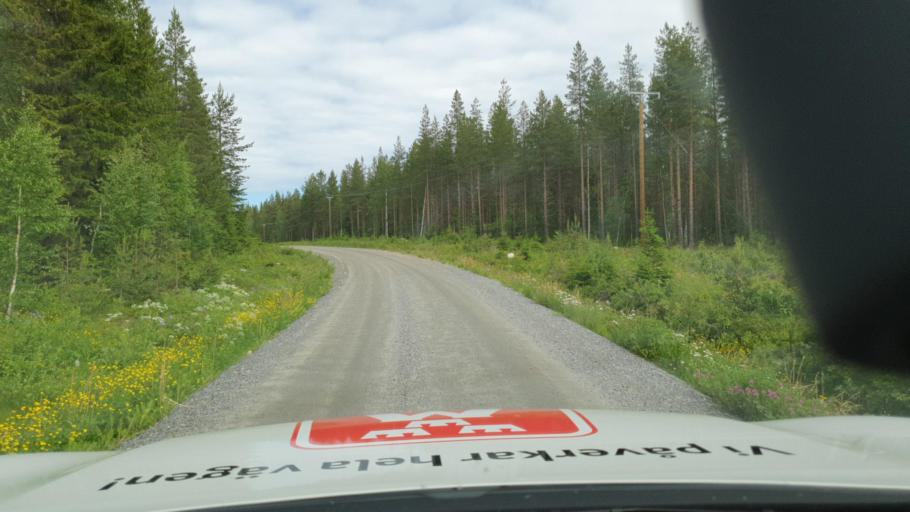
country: SE
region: Vaesterbotten
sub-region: Skelleftea Kommun
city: Langsele
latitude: 64.5493
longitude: 20.2846
